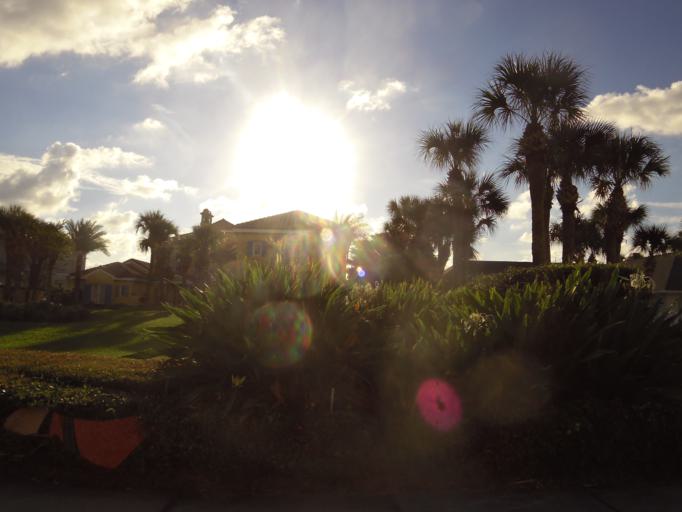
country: US
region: Florida
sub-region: Saint Johns County
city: Ponte Vedra Beach
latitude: 30.2248
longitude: -81.3739
